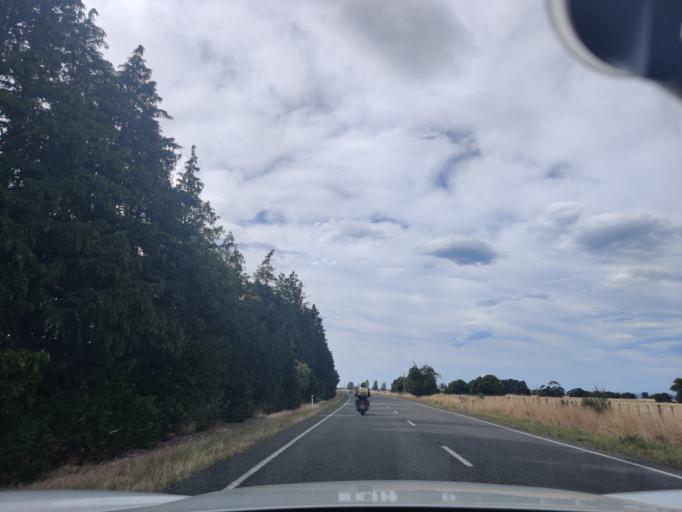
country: NZ
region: Wellington
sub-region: Masterton District
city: Masterton
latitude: -40.8695
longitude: 175.6475
